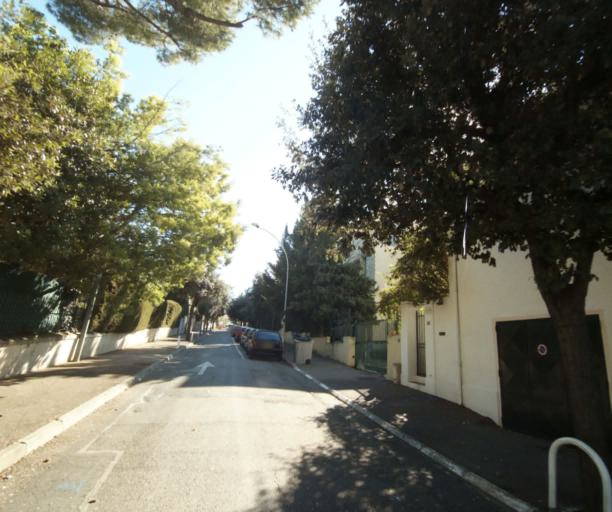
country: FR
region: Provence-Alpes-Cote d'Azur
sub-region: Departement des Alpes-Maritimes
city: Antibes
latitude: 43.5656
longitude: 7.1181
